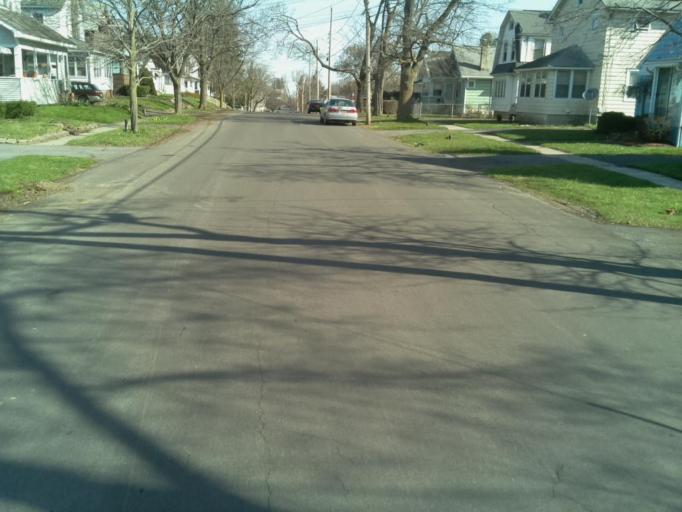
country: US
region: New York
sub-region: Onondaga County
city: Lyncourt
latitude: 43.0659
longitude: -76.1072
